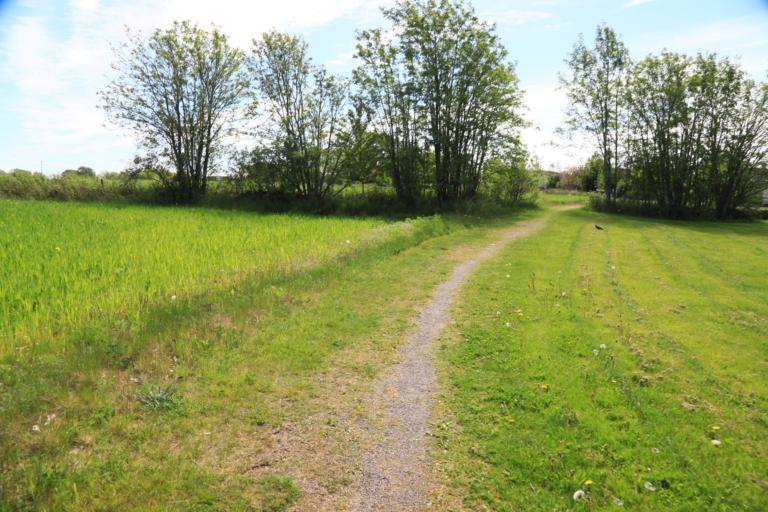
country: SE
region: Halland
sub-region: Varbergs Kommun
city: Traslovslage
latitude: 57.1142
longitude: 12.3024
